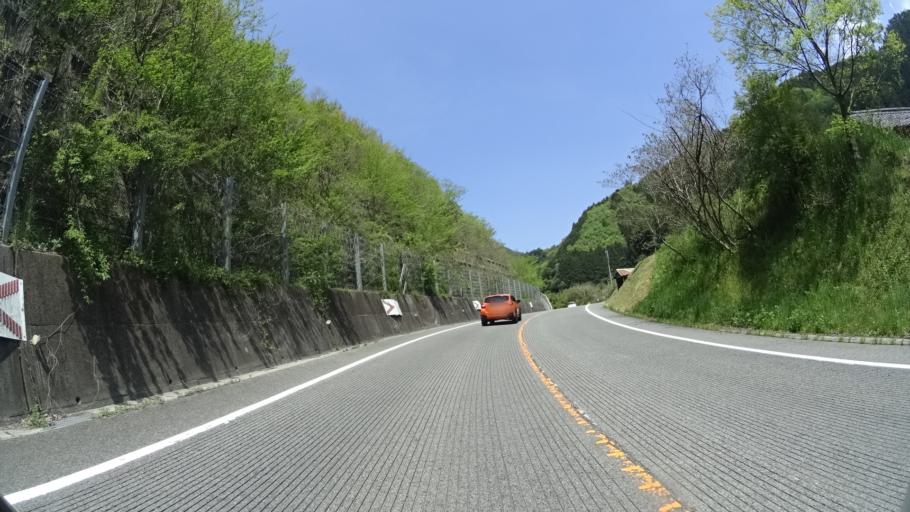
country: JP
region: Ehime
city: Hojo
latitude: 33.9253
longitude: 132.8900
